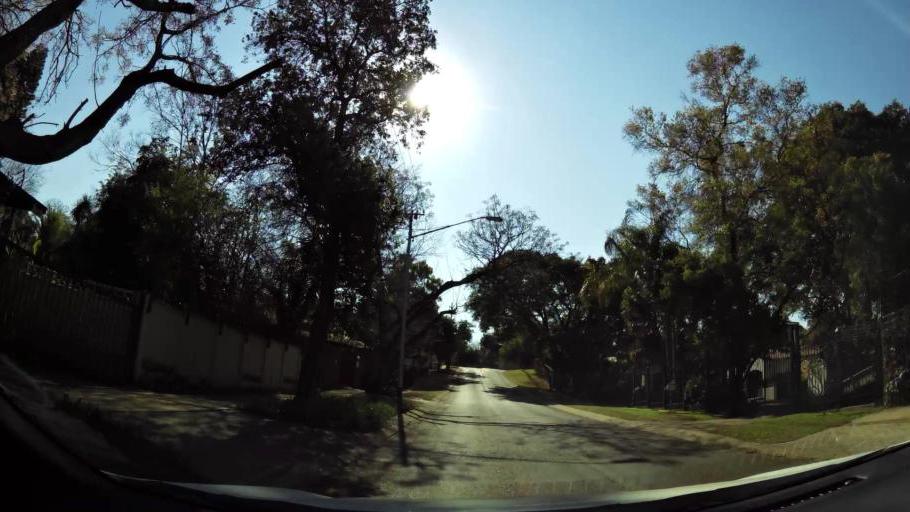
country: ZA
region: Gauteng
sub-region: City of Tshwane Metropolitan Municipality
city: Pretoria
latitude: -25.7776
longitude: 28.2630
